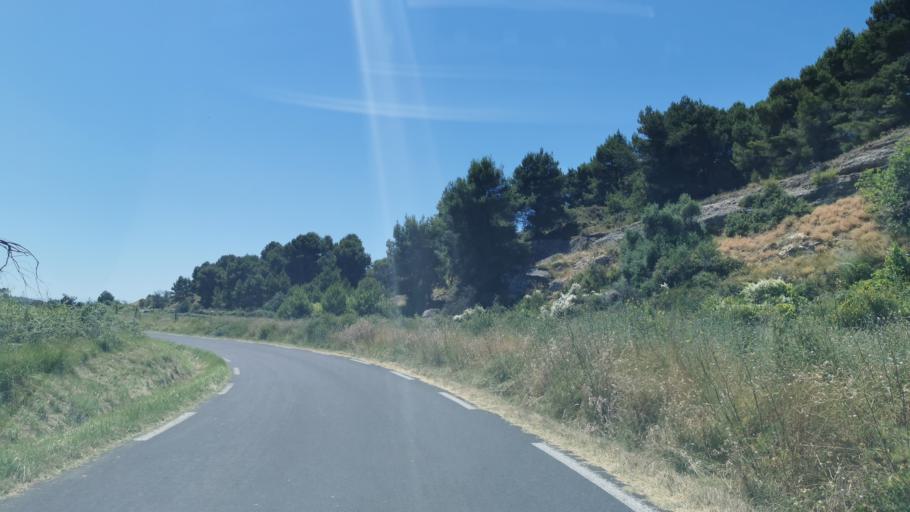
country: FR
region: Languedoc-Roussillon
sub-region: Departement de l'Herault
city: Nissan-lez-Enserune
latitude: 43.2683
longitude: 3.1244
